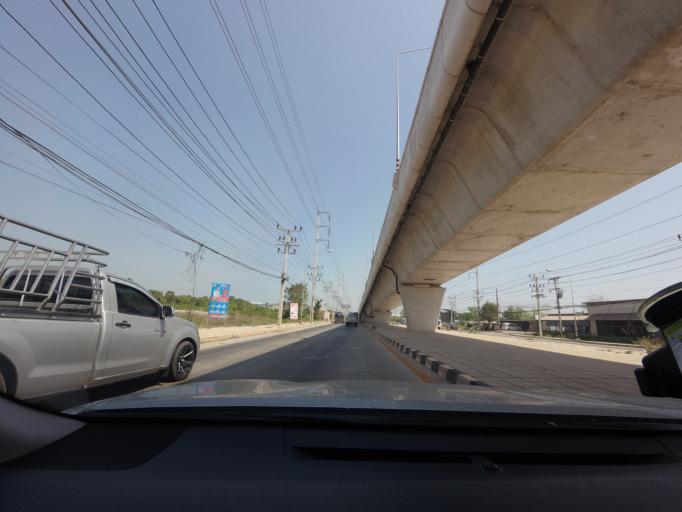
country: TH
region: Surat Thani
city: Surat Thani
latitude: 9.1540
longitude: 99.3694
